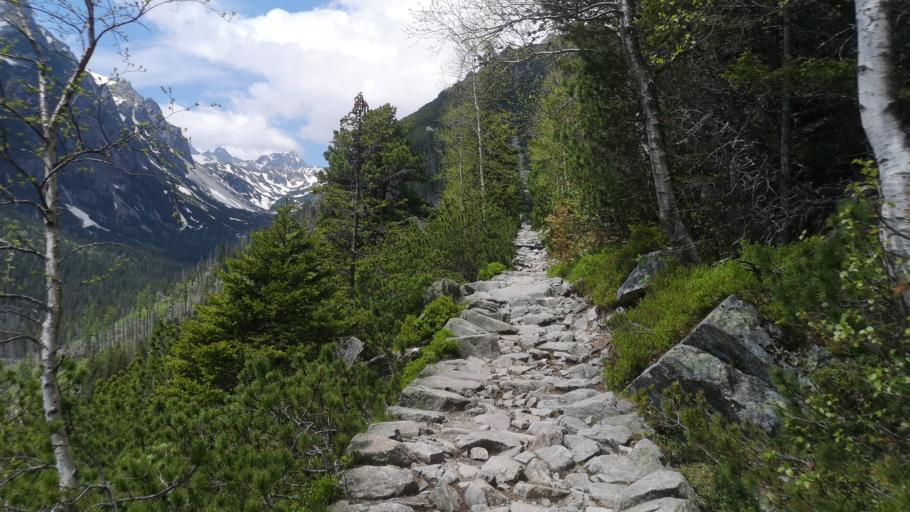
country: SK
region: Presovsky
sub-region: Okres Poprad
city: Vysoke Tatry
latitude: 49.1704
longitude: 20.2229
